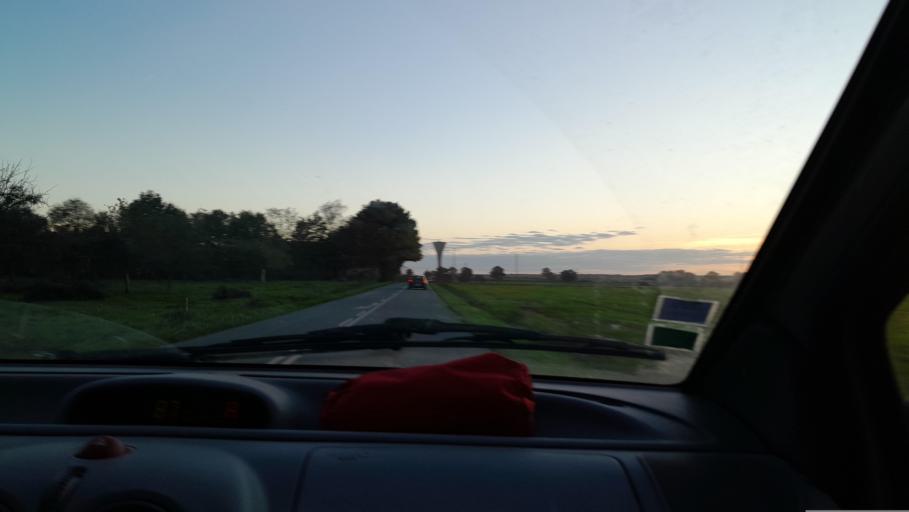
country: FR
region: Pays de la Loire
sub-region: Departement de la Mayenne
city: Ballots
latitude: 47.9206
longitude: -1.0958
